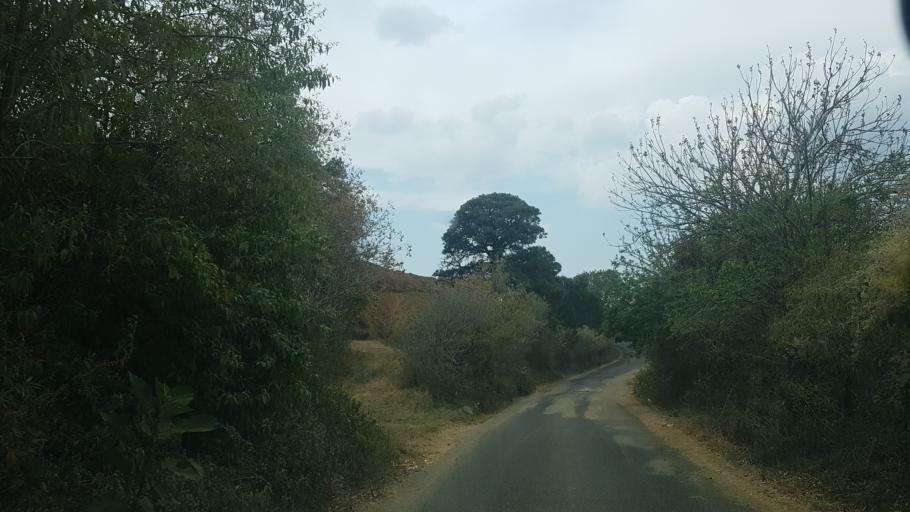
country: MX
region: Puebla
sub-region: Atzitzihuacan
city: Santiago Atzitzihuacan
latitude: 18.8384
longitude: -98.6161
